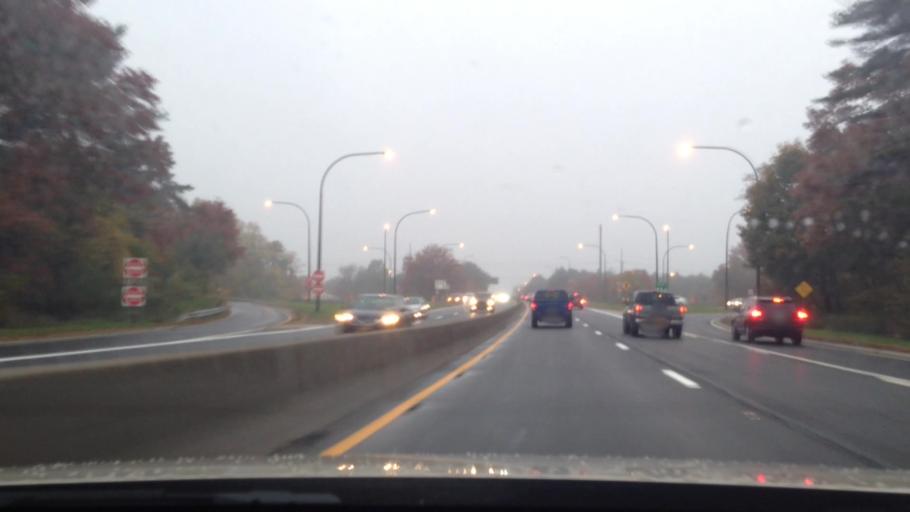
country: US
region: New York
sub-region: Suffolk County
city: Bay Wood
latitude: 40.7691
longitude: -73.2798
